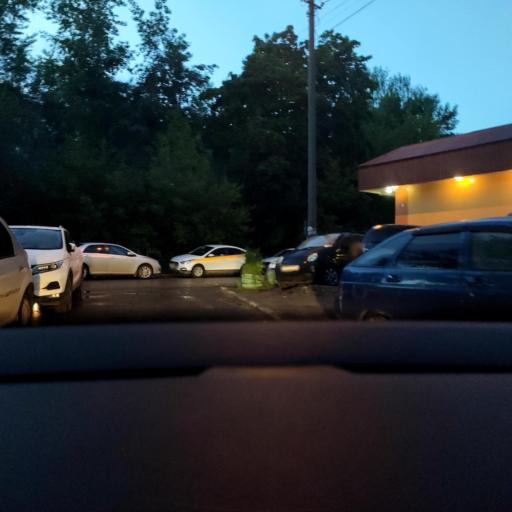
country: RU
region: Moskovskaya
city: Reutov
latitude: 55.7783
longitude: 37.8945
